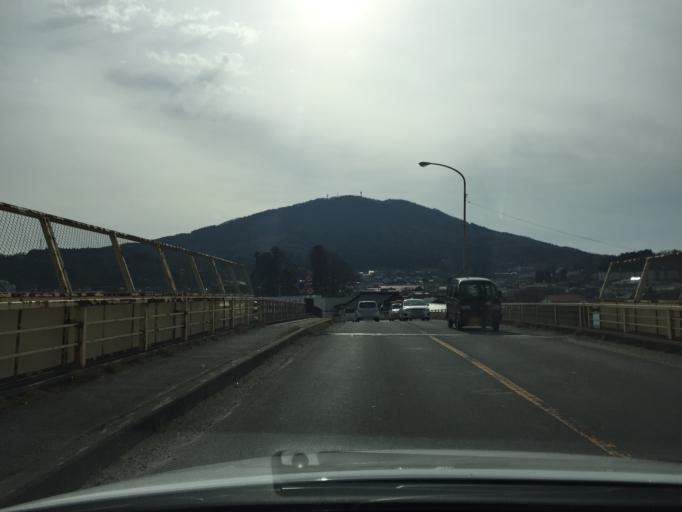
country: JP
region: Fukushima
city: Funehikimachi-funehiki
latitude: 37.4444
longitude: 140.5728
